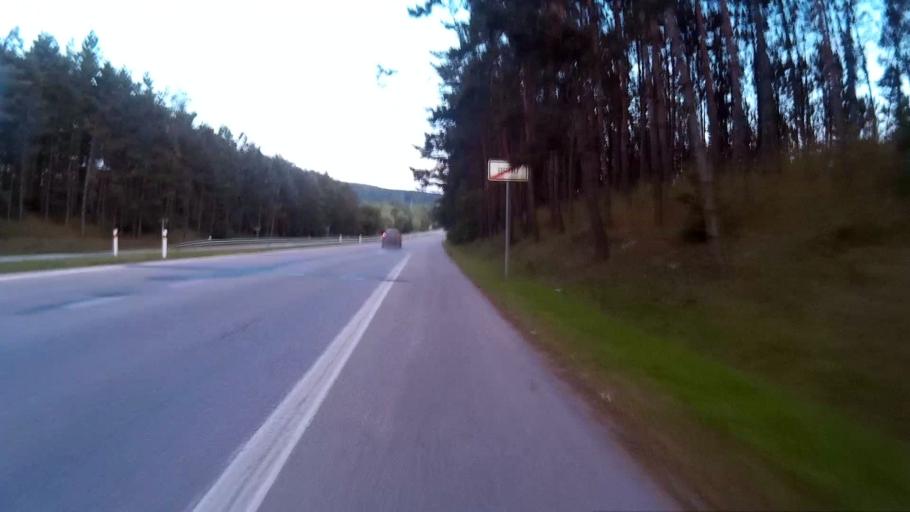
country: CZ
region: South Moravian
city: Troubsko
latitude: 49.2146
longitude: 16.5216
